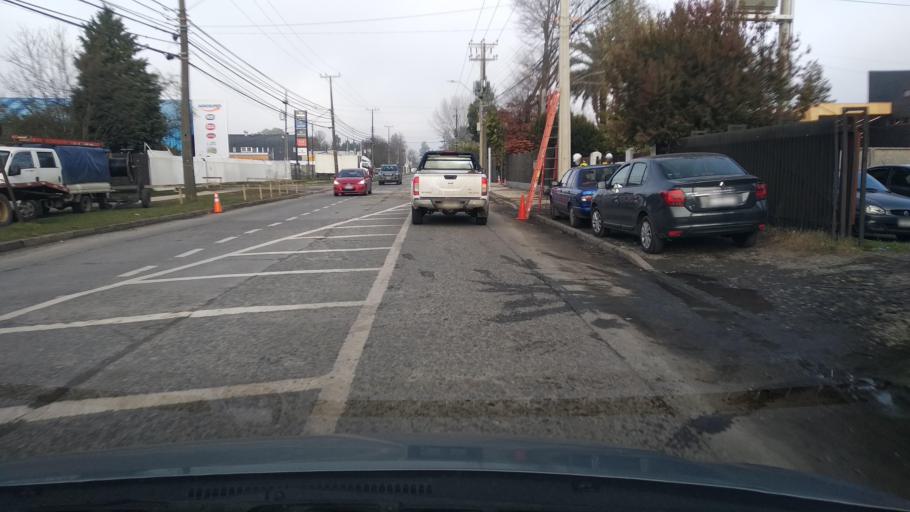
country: CL
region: Los Rios
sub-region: Provincia de Valdivia
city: Valdivia
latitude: -39.8084
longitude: -73.2348
